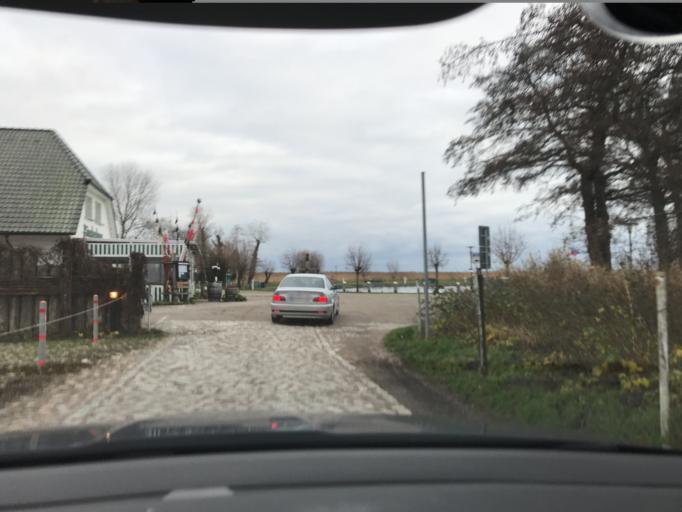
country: DE
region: Mecklenburg-Vorpommern
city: Ostseebad Dierhagen
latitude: 54.3726
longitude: 12.4181
